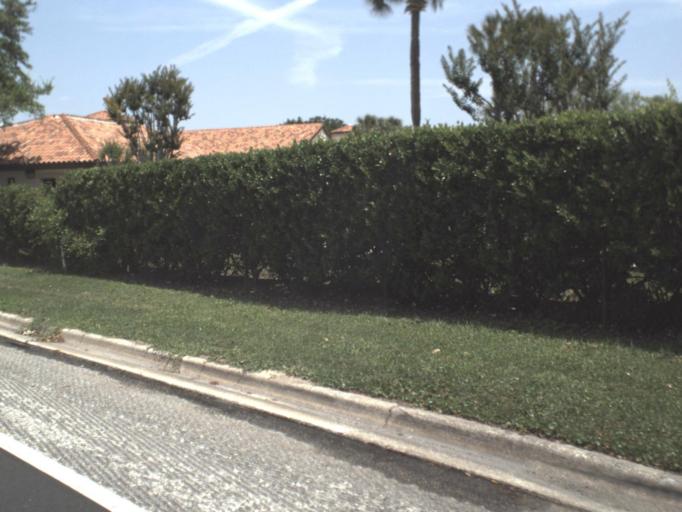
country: US
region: Florida
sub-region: Duval County
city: Jacksonville
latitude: 30.2408
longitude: -81.6243
